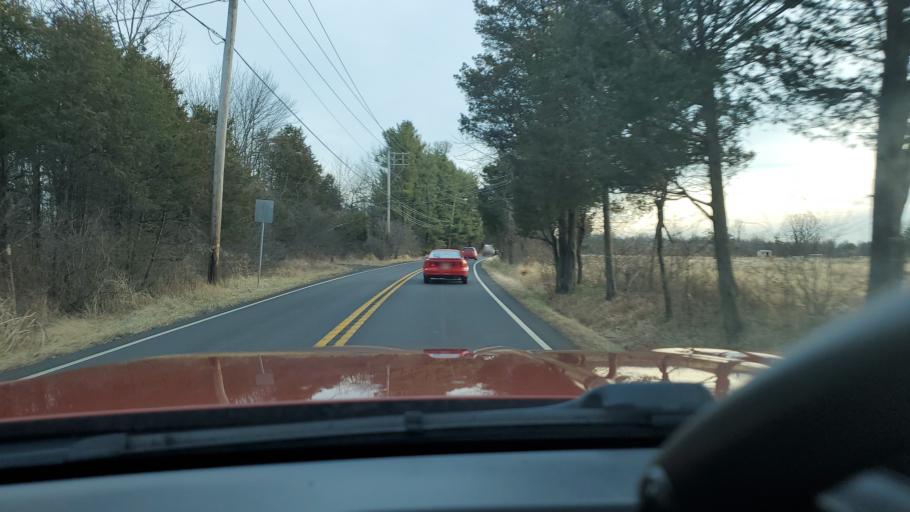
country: US
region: Pennsylvania
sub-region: Montgomery County
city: Telford
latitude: 40.3558
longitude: -75.3607
